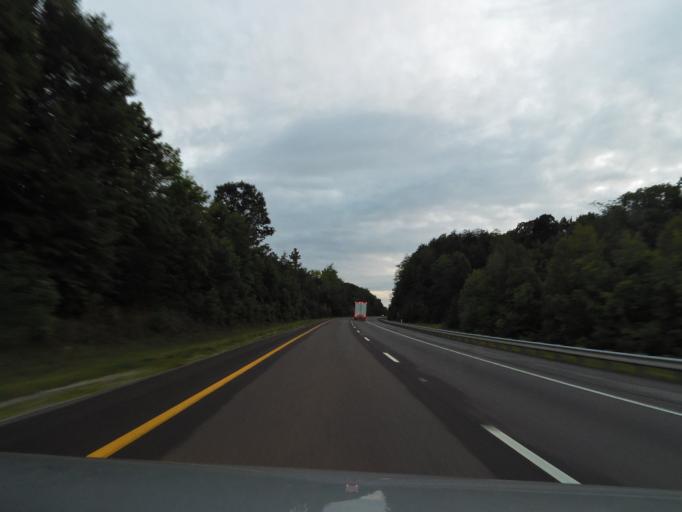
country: US
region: Tennessee
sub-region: Campbell County
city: Jacksboro
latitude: 36.4504
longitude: -84.2663
